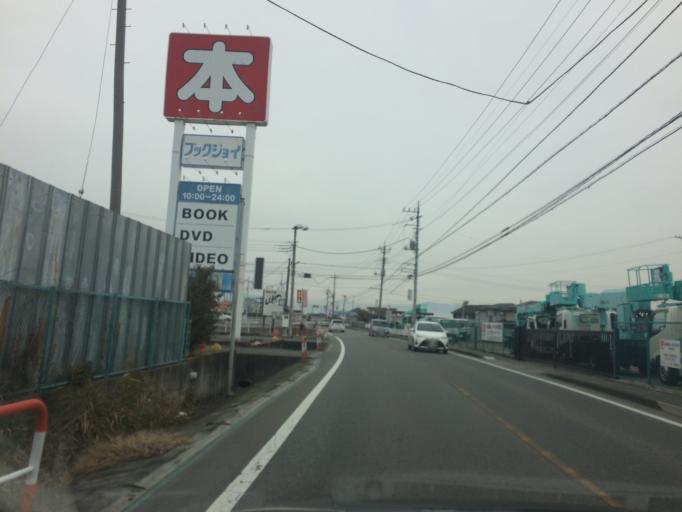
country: JP
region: Yamanashi
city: Ryuo
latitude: 35.5742
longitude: 138.4856
